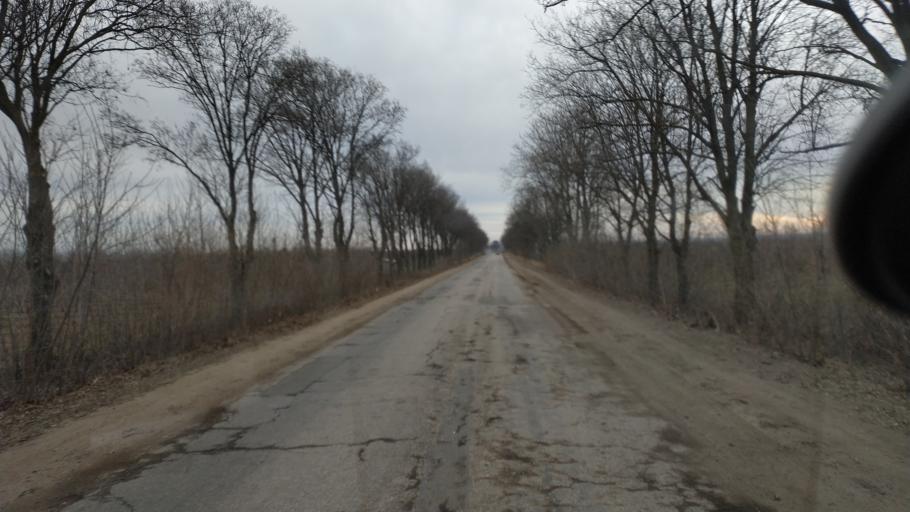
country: MD
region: Telenesti
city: Cocieri
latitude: 47.2656
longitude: 29.1030
